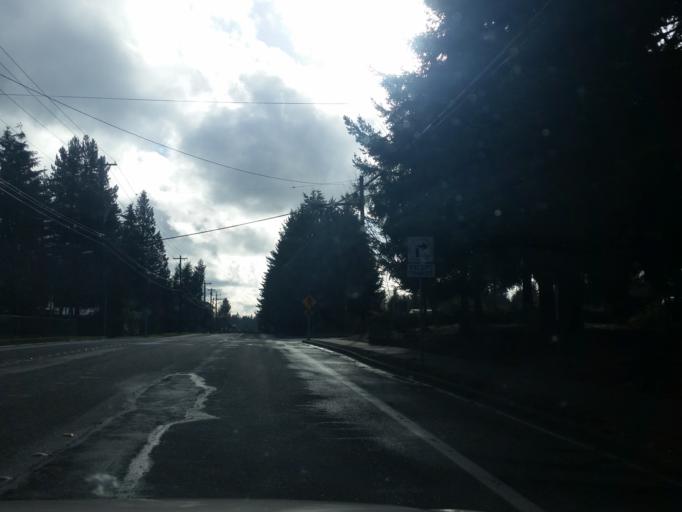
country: US
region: Washington
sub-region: Snohomish County
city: Lynnwood
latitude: 47.8166
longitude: -122.3249
